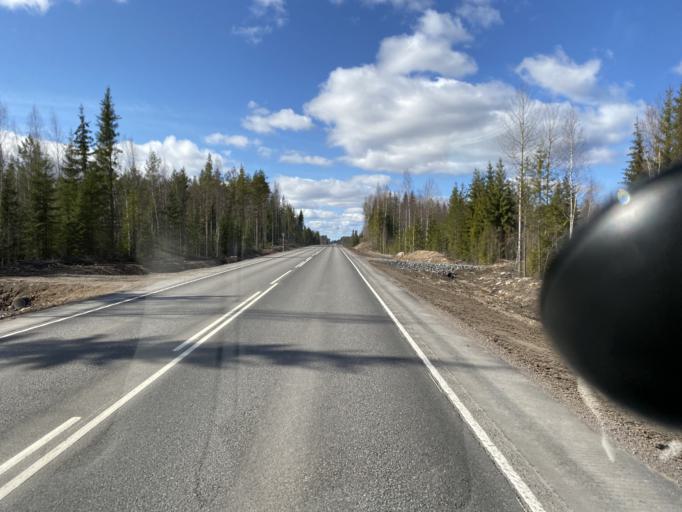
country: FI
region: Satakunta
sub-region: Pori
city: Kokemaeki
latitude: 61.1724
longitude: 22.5061
